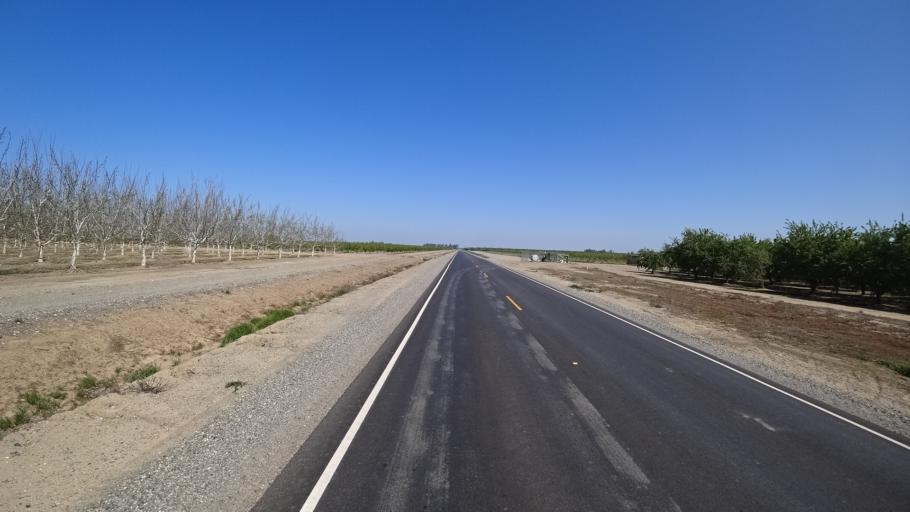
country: US
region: California
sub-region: Glenn County
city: Hamilton City
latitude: 39.6408
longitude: -122.0650
